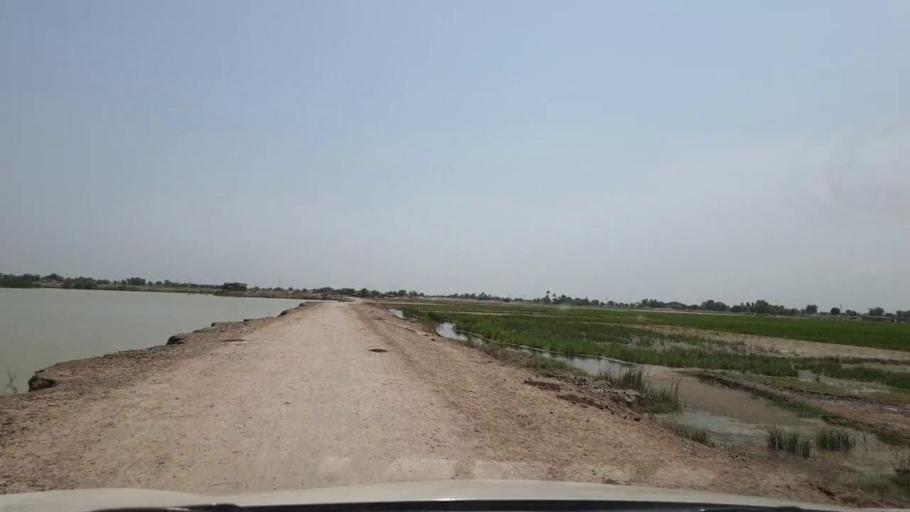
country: PK
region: Sindh
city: Ratodero
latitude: 27.8081
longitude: 68.2444
